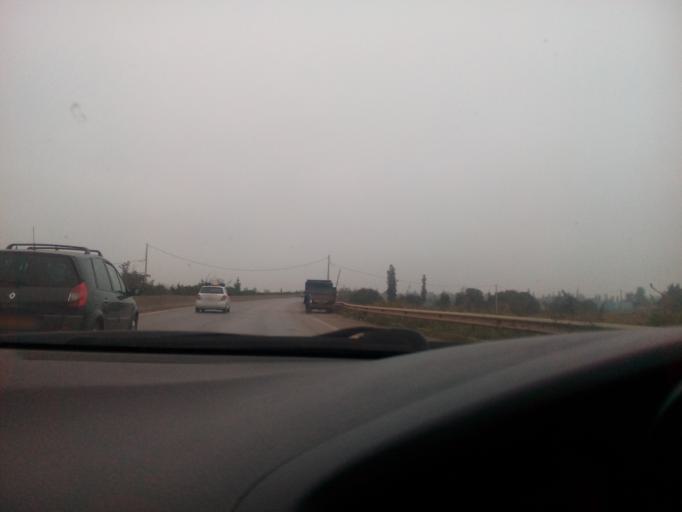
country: DZ
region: Oran
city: Bou Tlelis
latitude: 35.5681
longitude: -0.9102
